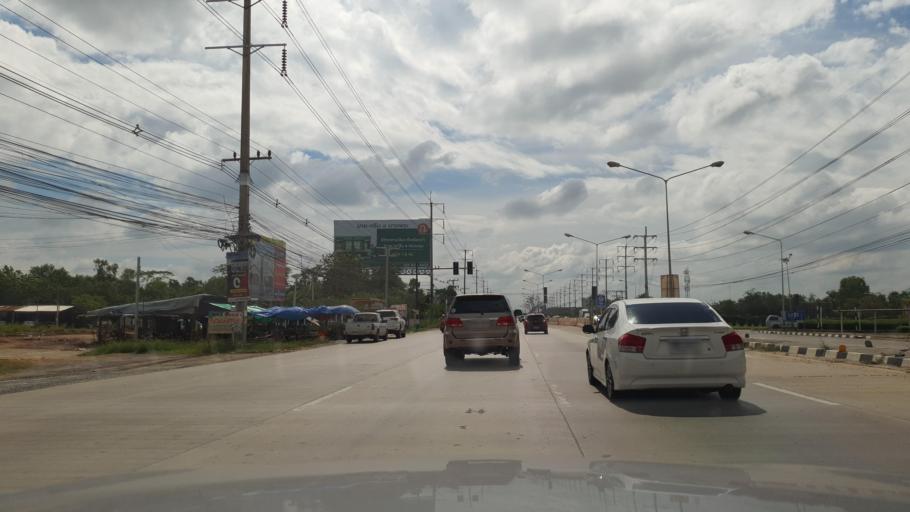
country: TH
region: Chachoengsao
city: Ban Pho
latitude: 13.6111
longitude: 101.0254
